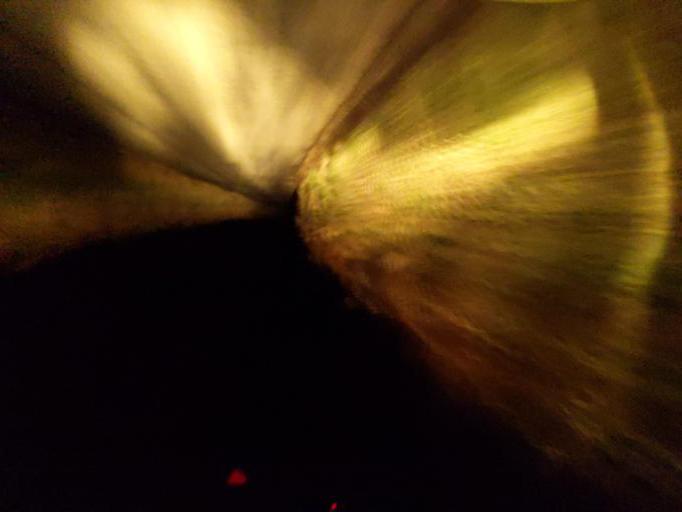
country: GB
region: England
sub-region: Cornwall
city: Torpoint
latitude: 50.3556
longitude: -4.2475
